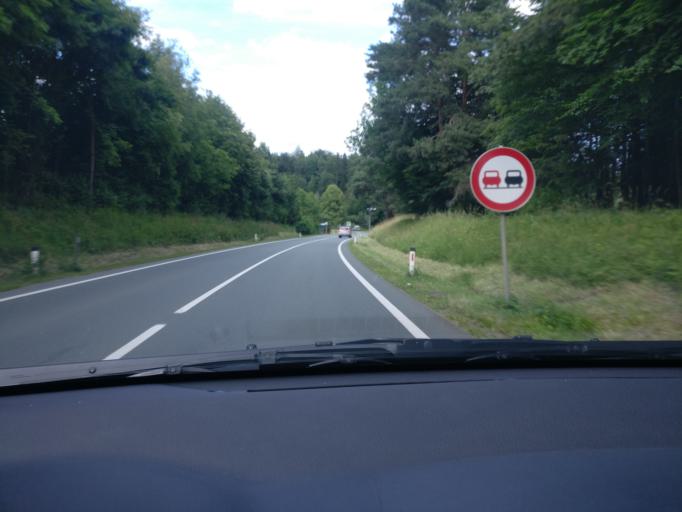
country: AT
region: Styria
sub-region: Politischer Bezirk Weiz
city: Hirnsdorf
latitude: 47.1889
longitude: 15.8152
